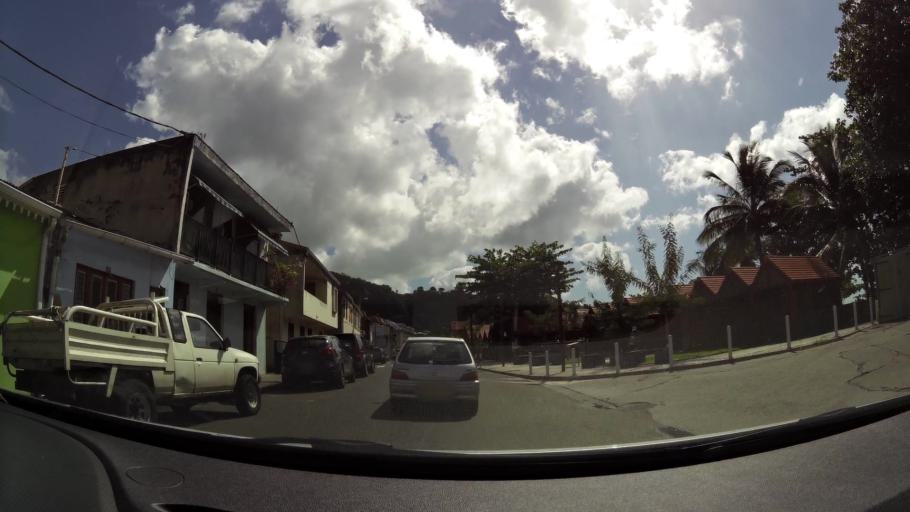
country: MQ
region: Martinique
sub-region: Martinique
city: Saint-Pierre
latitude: 14.7476
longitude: -61.1779
